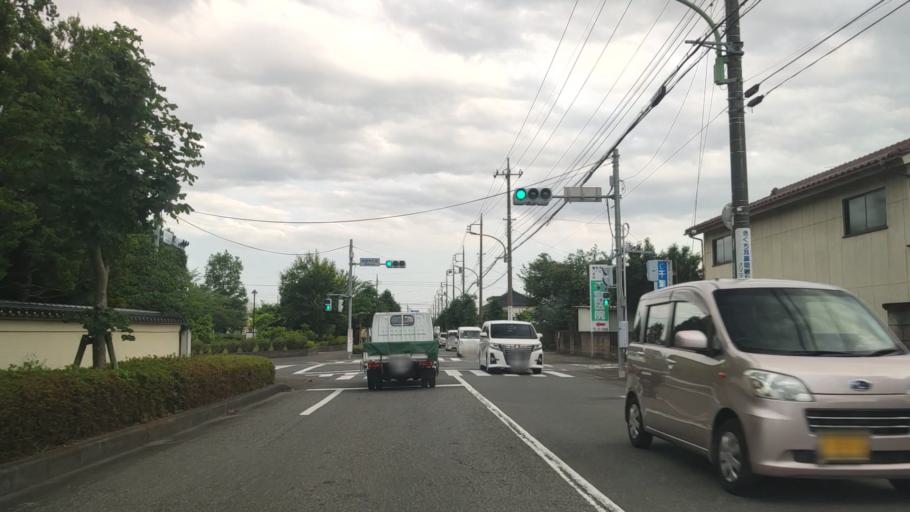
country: JP
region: Tokyo
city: Ome
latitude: 35.7898
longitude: 139.2989
